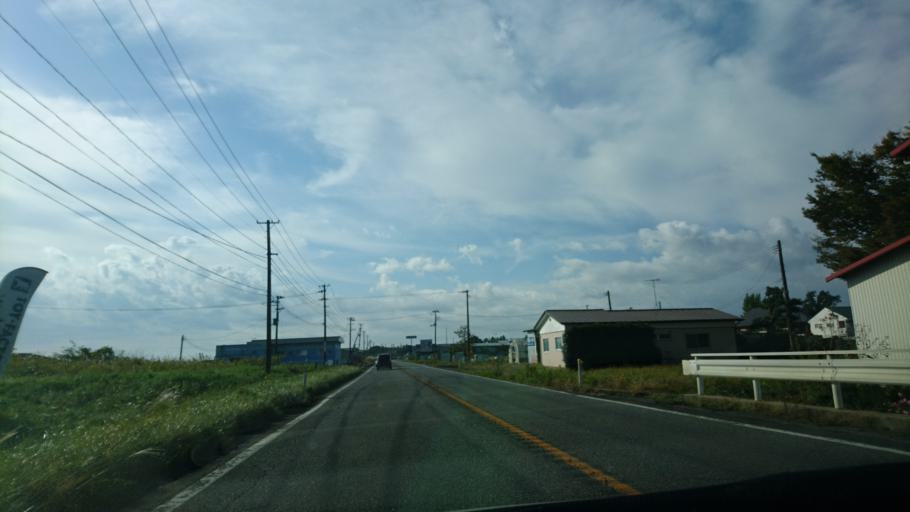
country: JP
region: Miyagi
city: Furukawa
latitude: 38.6123
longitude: 140.9833
